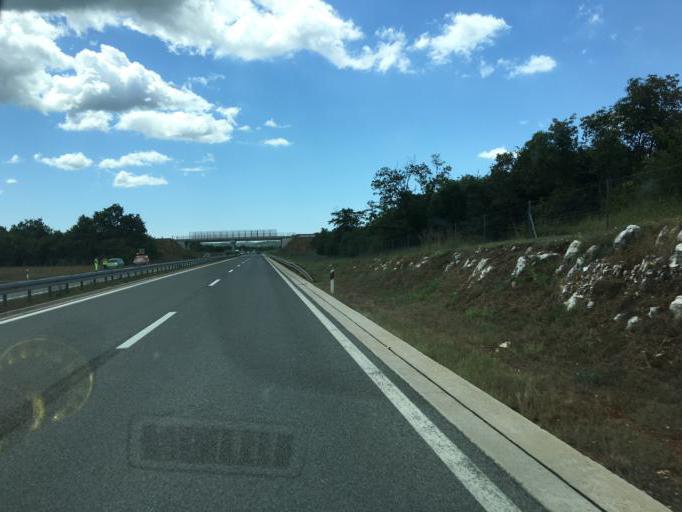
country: HR
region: Istarska
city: Vrsar
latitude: 45.1834
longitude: 13.7324
